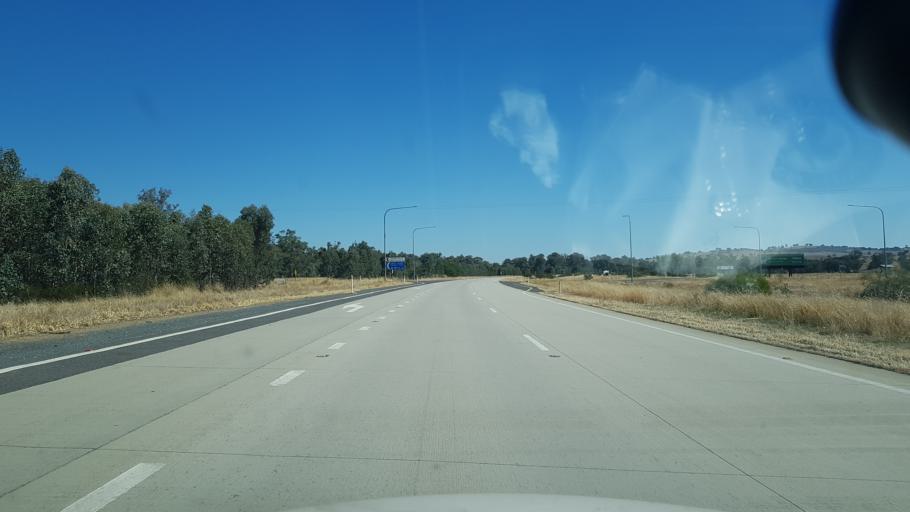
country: AU
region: New South Wales
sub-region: Greater Hume Shire
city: Holbrook
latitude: -35.9107
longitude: 147.1553
